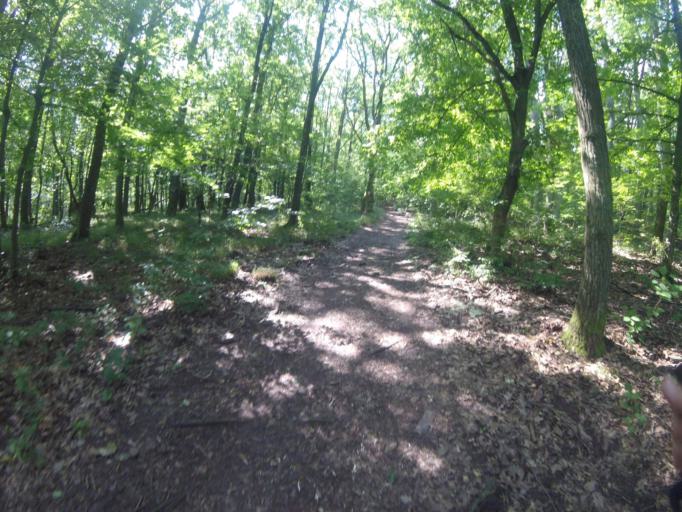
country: SK
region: Nitriansky
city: Sahy
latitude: 47.9871
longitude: 18.8894
